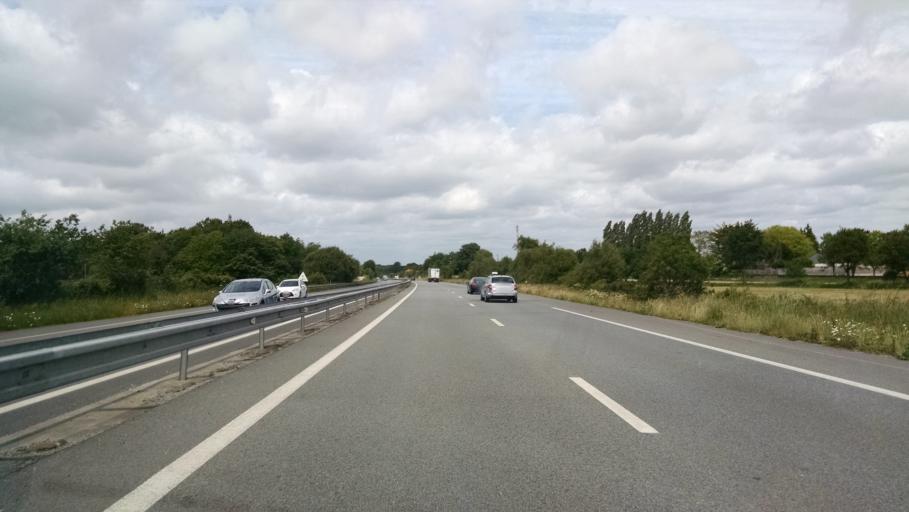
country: FR
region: Brittany
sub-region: Departement du Morbihan
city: Brech
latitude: 47.6963
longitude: -3.0371
